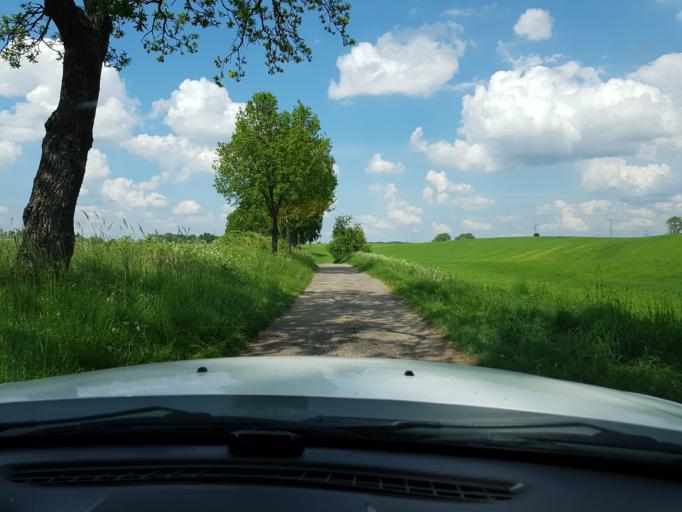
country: PL
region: West Pomeranian Voivodeship
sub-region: Powiat drawski
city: Drawsko Pomorskie
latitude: 53.5210
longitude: 15.7506
